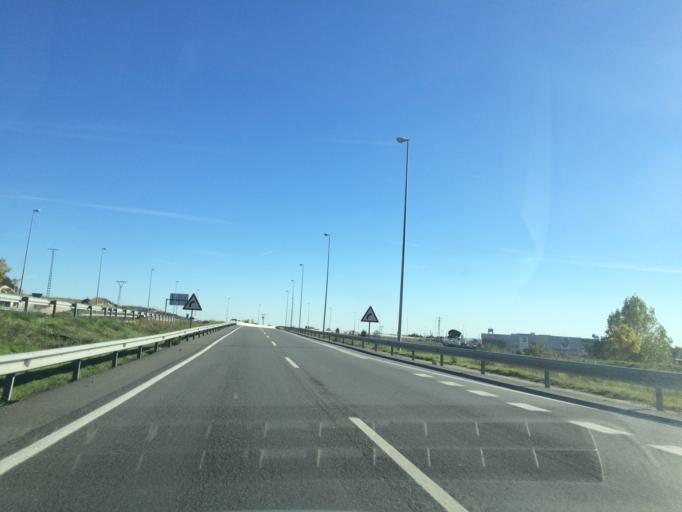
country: ES
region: Madrid
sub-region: Provincia de Madrid
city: Colmenar Viejo
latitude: 40.6462
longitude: -3.7335
